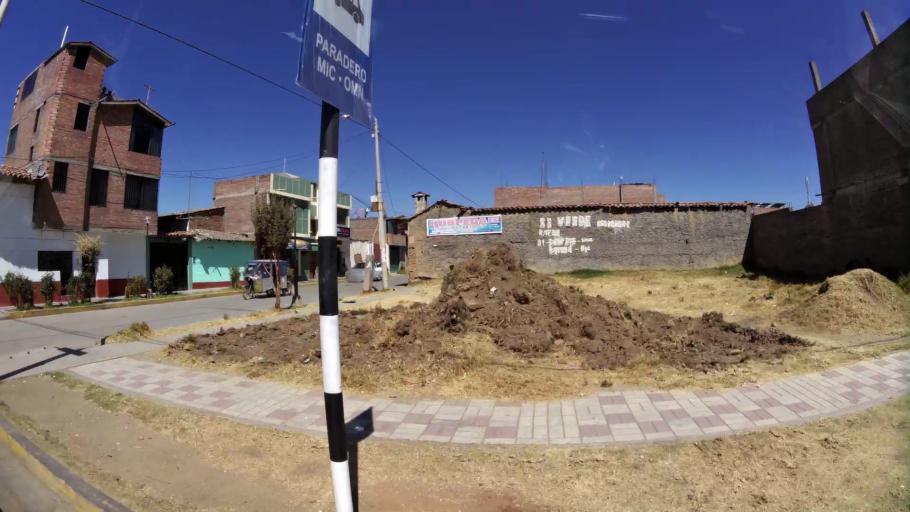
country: PE
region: Junin
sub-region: Provincia de Concepcion
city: Concepcion
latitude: -11.9148
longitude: -75.3162
